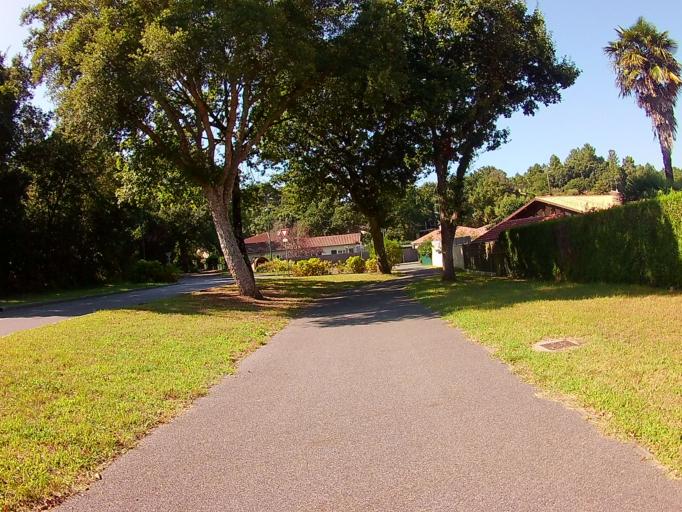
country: FR
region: Aquitaine
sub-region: Departement des Landes
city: Labenne
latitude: 43.5882
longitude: -1.4322
